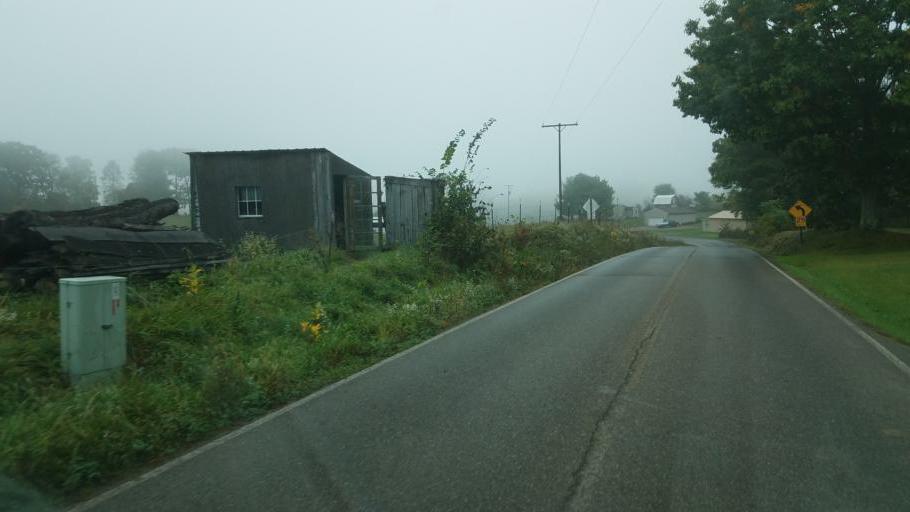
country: US
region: Ohio
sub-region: Harrison County
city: Cadiz
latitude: 40.3852
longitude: -81.1199
